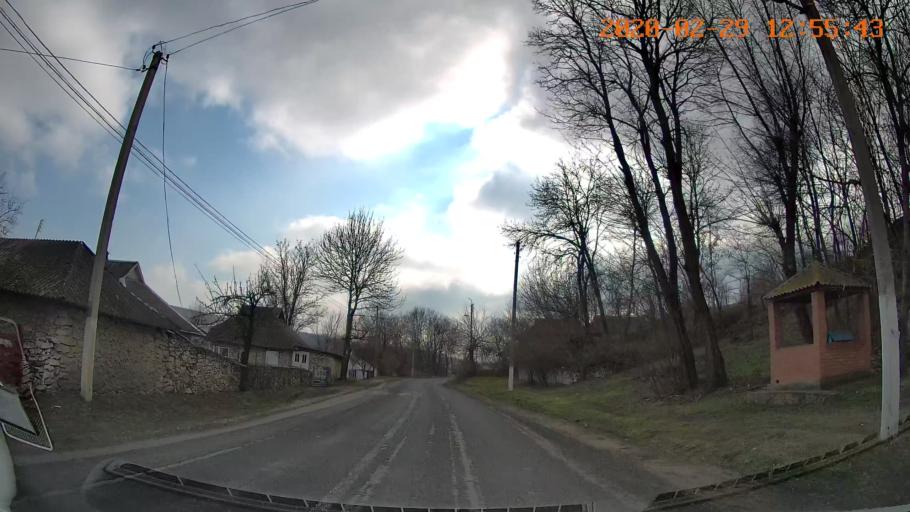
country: MD
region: Telenesti
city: Camenca
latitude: 48.0924
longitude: 28.7242
